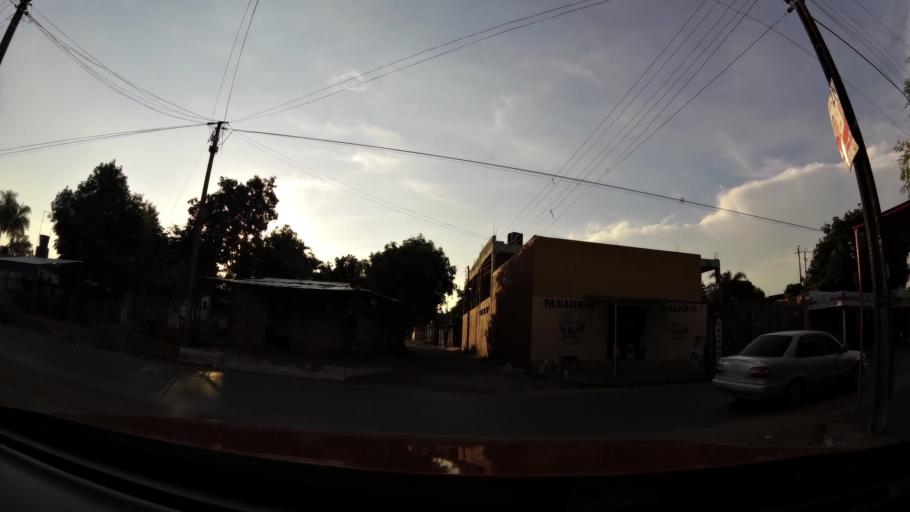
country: PY
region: Central
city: San Lorenzo
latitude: -25.3596
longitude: -57.5058
